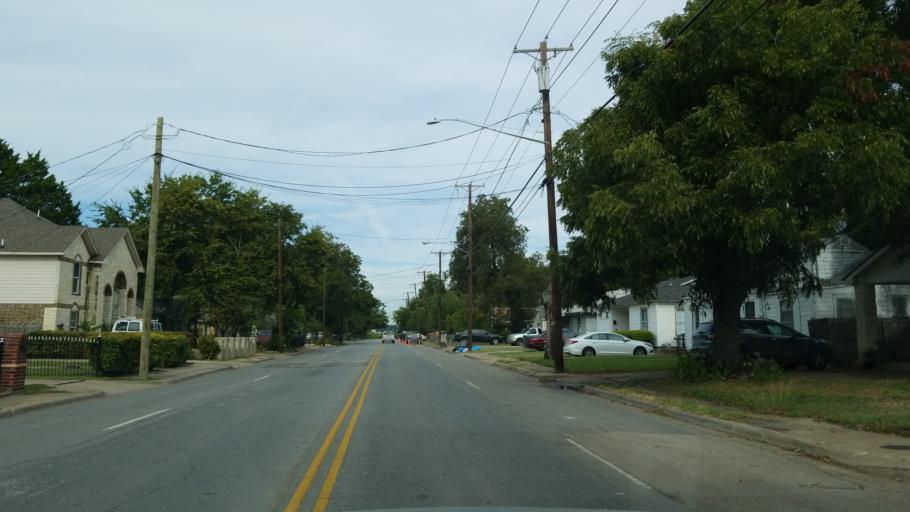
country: US
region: Texas
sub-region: Dallas County
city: Dallas
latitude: 32.7816
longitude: -96.7194
